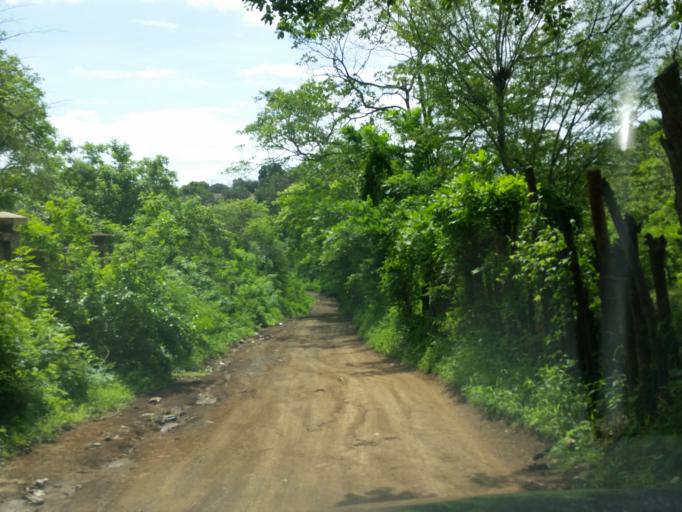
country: NI
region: Managua
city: Managua
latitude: 12.0887
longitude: -86.2504
